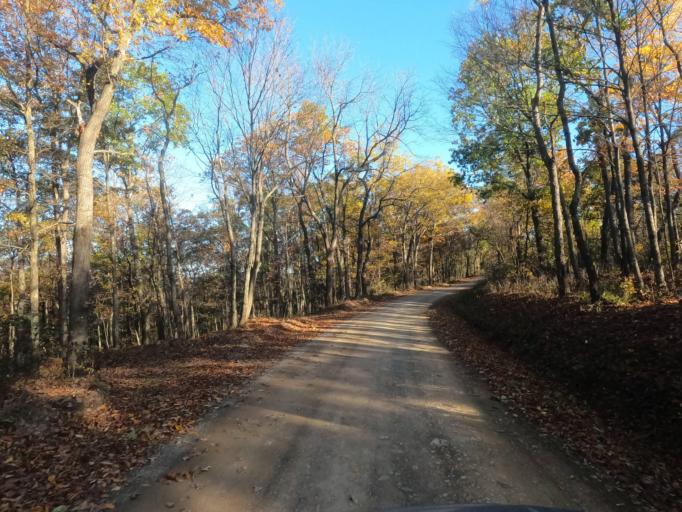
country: US
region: West Virginia
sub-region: Mineral County
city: Fort Ashby
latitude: 39.5647
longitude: -78.5214
